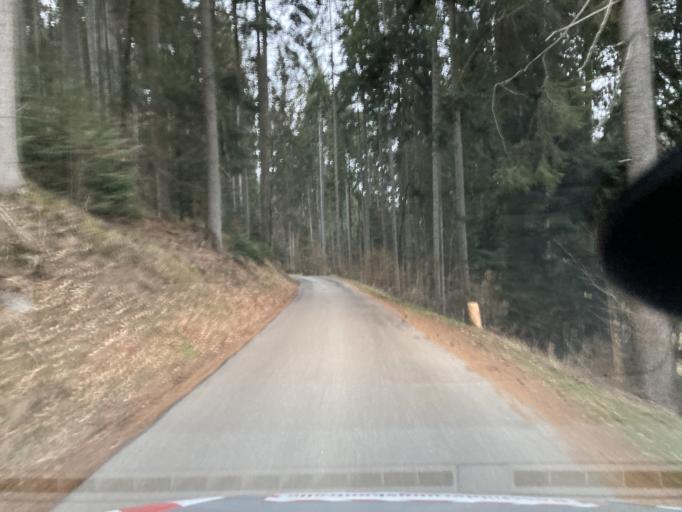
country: DE
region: Baden-Wuerttemberg
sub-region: Karlsruhe Region
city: Neubulach
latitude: 48.6618
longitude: 8.6559
